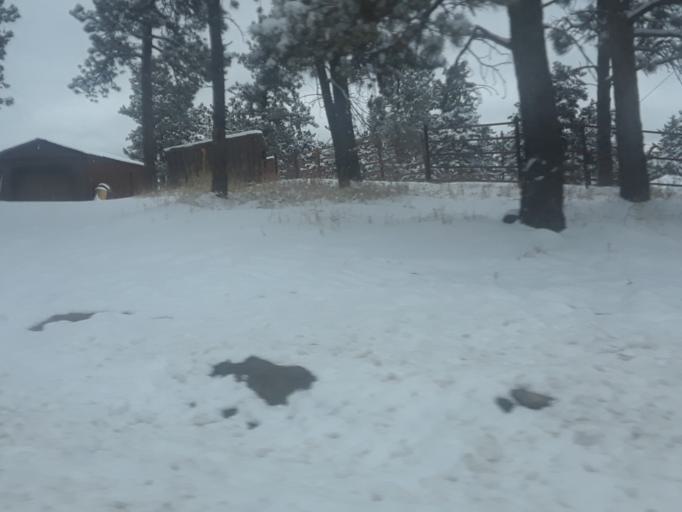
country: US
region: Colorado
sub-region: Boulder County
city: Coal Creek
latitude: 39.9203
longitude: -105.3653
